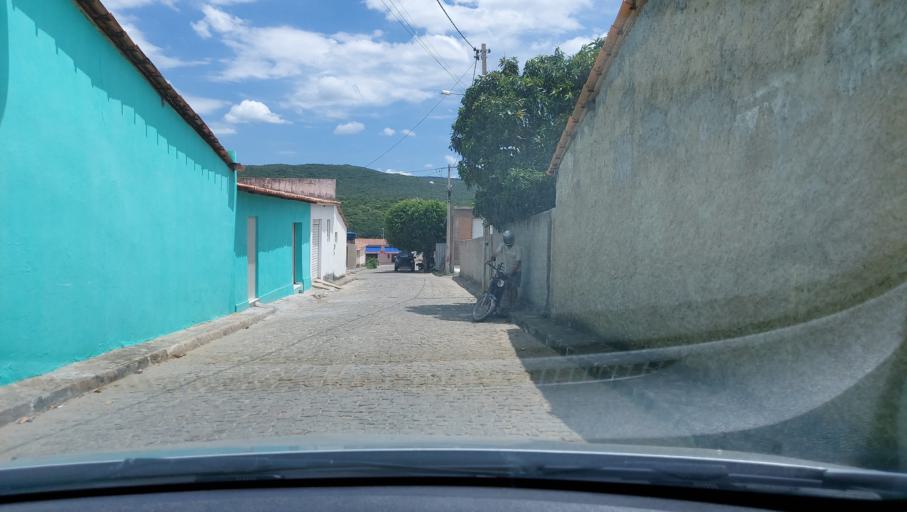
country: BR
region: Bahia
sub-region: Oliveira Dos Brejinhos
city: Beira Rio
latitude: -11.9979
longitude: -42.6292
